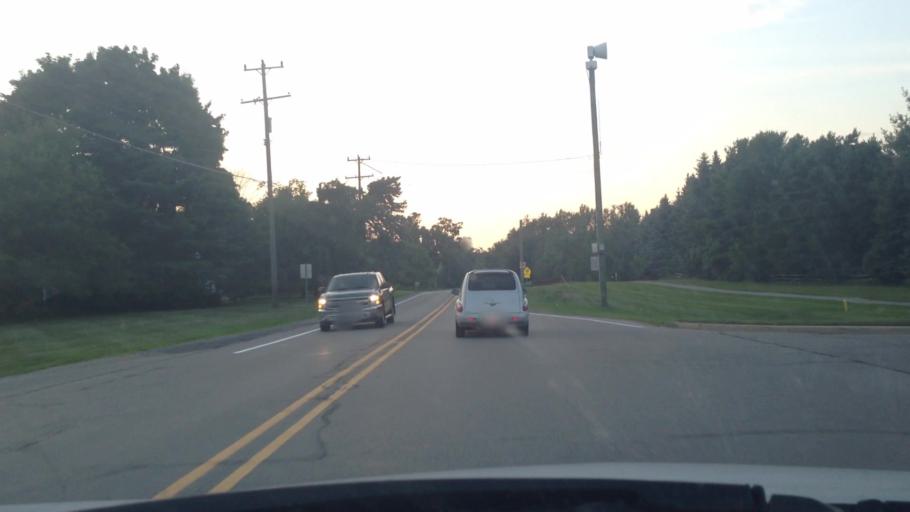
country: US
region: Michigan
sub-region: Oakland County
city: Lake Orion
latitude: 42.7482
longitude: -83.3084
